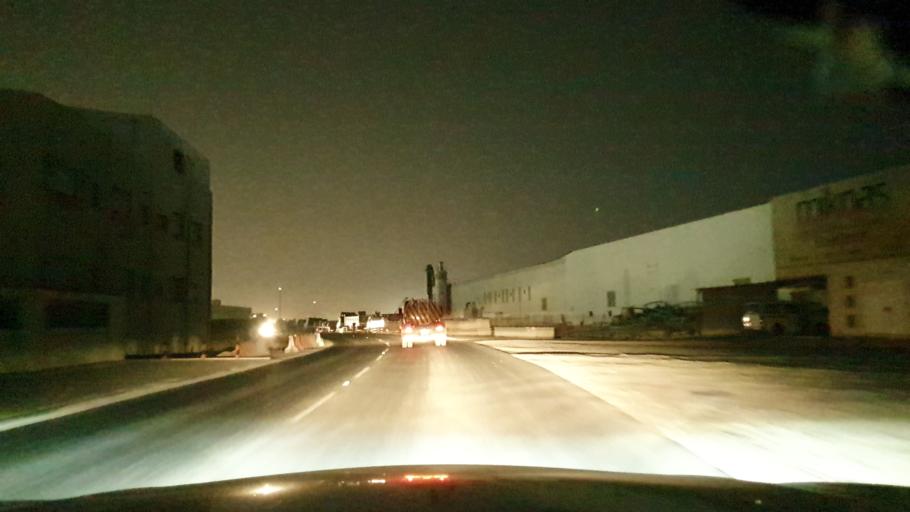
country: BH
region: Northern
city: Sitrah
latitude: 26.0954
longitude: 50.6149
